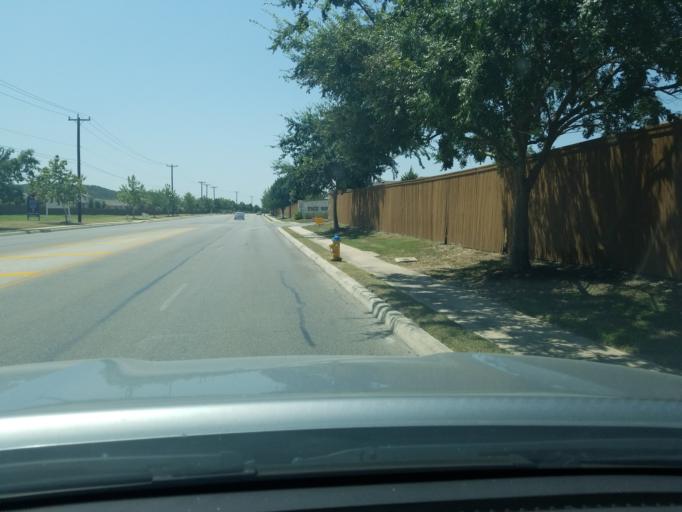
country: US
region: Texas
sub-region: Bexar County
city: Timberwood Park
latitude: 29.7059
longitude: -98.4832
